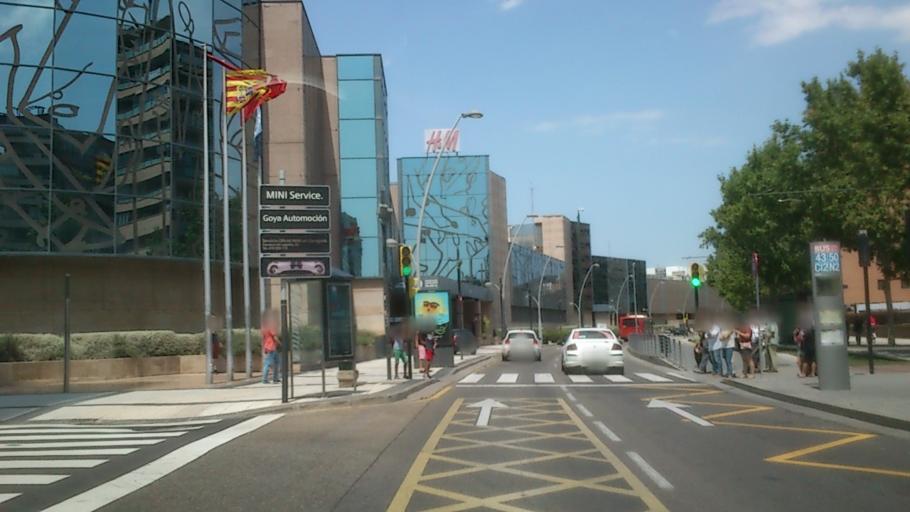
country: ES
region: Aragon
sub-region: Provincia de Zaragoza
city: Almozara
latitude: 41.6690
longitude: -0.8885
